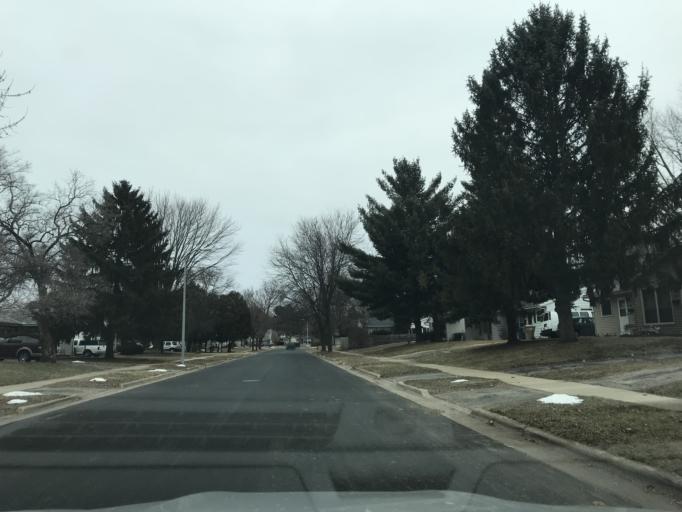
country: US
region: Wisconsin
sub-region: Dane County
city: Monona
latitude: 43.0865
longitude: -89.3044
